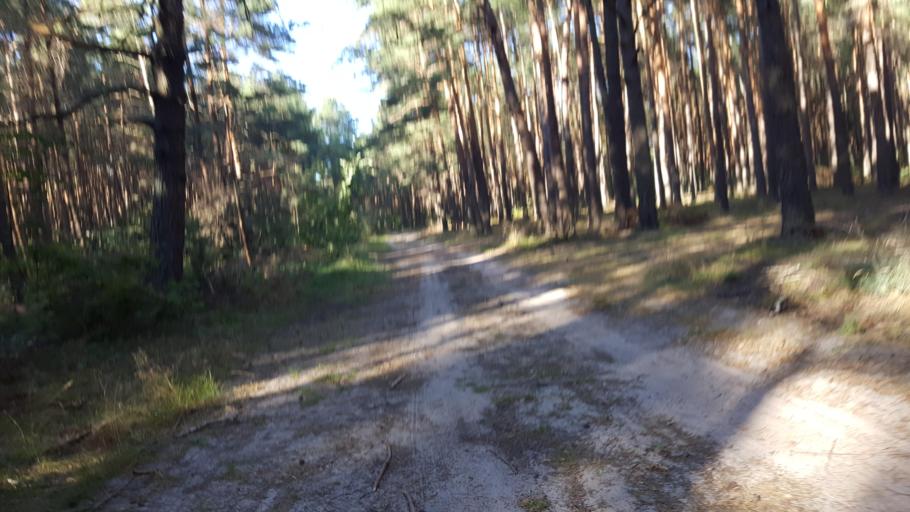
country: BY
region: Brest
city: Vysokaye
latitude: 52.3113
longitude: 23.2598
